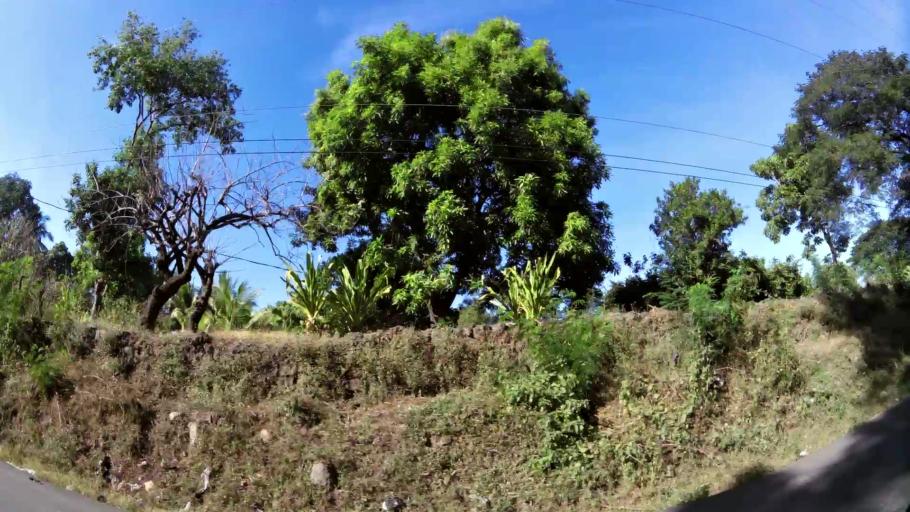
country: SV
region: San Miguel
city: San Miguel
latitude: 13.4773
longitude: -88.1963
